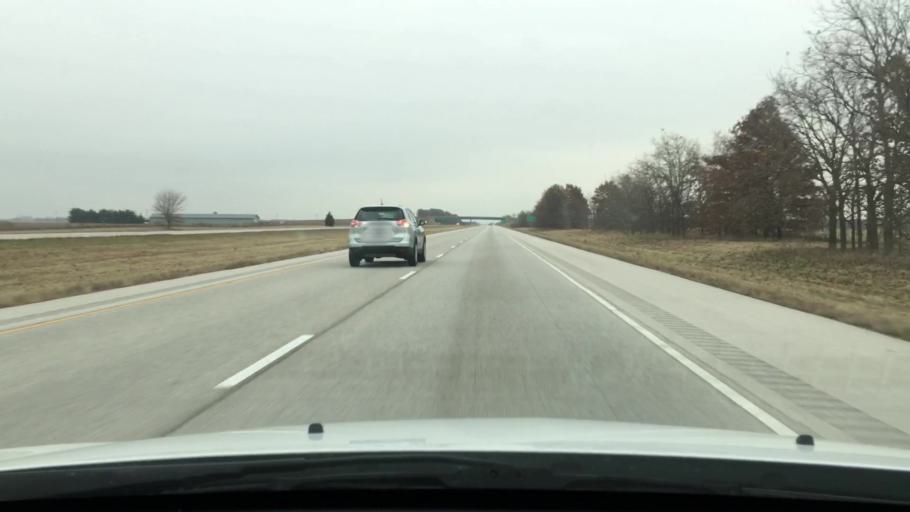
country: US
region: Illinois
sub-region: Morgan County
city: South Jacksonville
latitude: 39.6802
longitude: -90.3354
